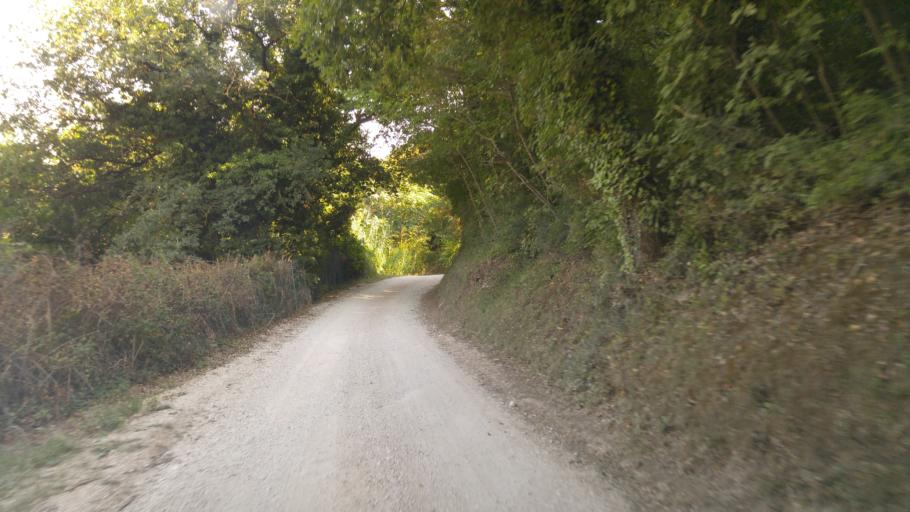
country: IT
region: The Marches
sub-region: Provincia di Pesaro e Urbino
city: Fossombrone
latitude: 43.6822
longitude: 12.7829
